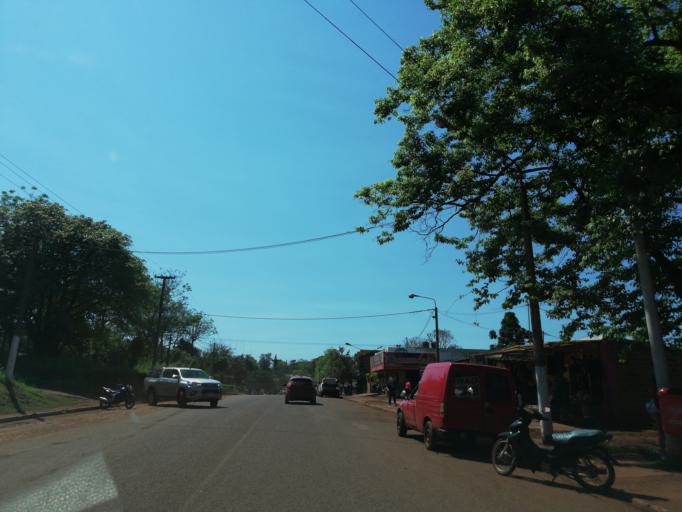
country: AR
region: Misiones
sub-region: Departamento de Eldorado
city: Eldorado
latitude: -26.4067
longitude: -54.6567
